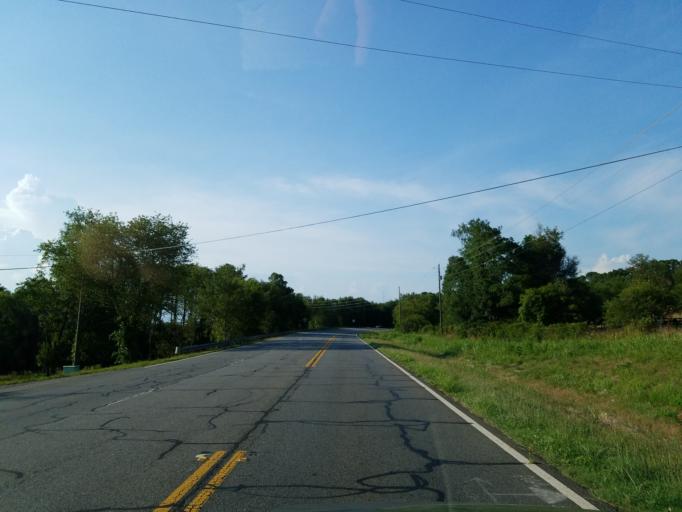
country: US
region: Georgia
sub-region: Bartow County
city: Rydal
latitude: 34.3799
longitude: -84.7094
